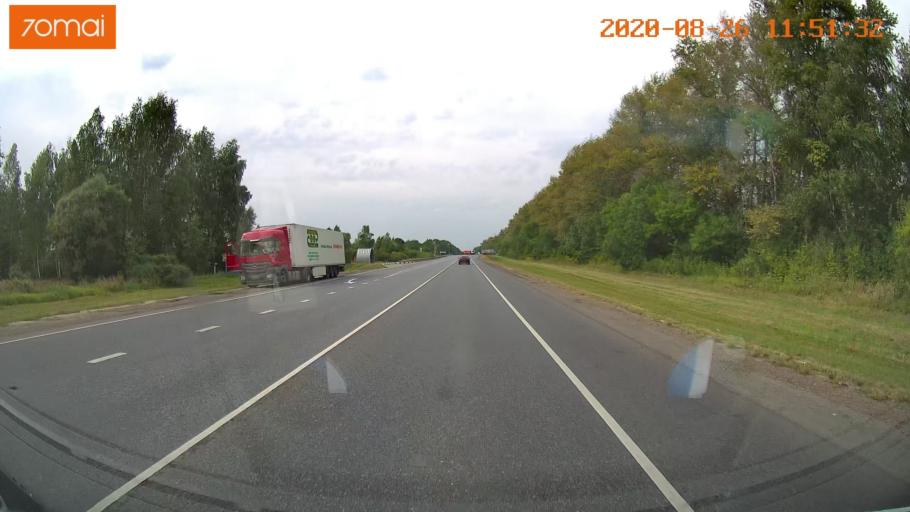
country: RU
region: Rjazan
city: Lesnoy
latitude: 54.2971
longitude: 40.4776
